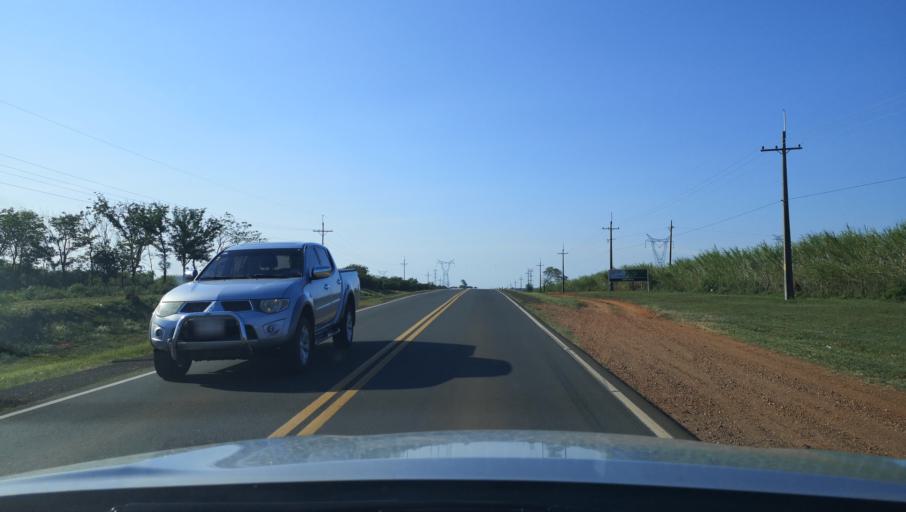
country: PY
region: Misiones
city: Santa Maria
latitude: -26.7967
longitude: -57.0228
